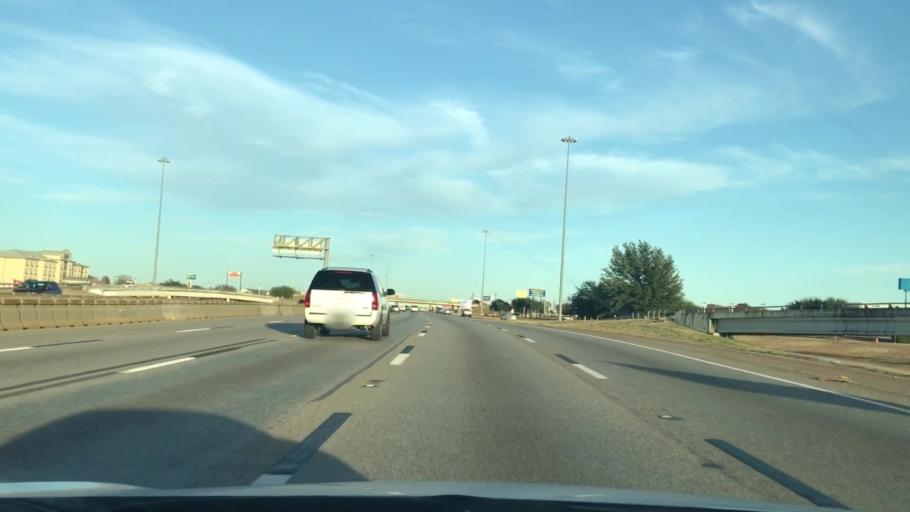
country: US
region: Texas
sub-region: Dallas County
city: Balch Springs
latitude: 32.7942
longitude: -96.6975
